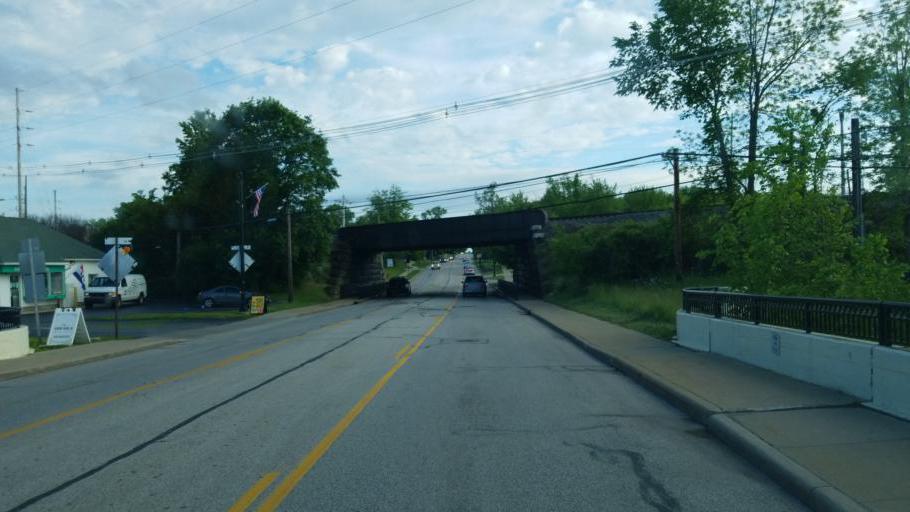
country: US
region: Ohio
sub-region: Summit County
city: Hudson
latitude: 41.2383
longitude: -81.4405
